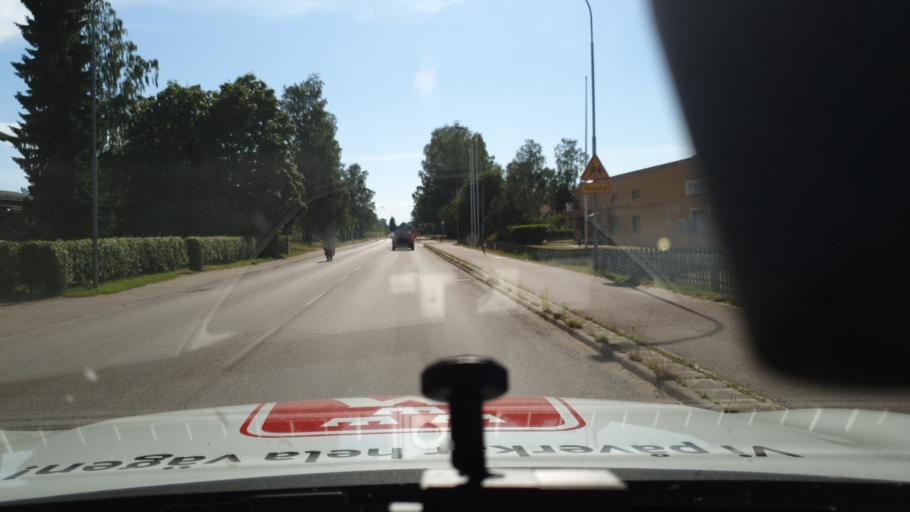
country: SE
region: Vaermland
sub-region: Kils Kommun
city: Kil
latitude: 59.5030
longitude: 13.3095
